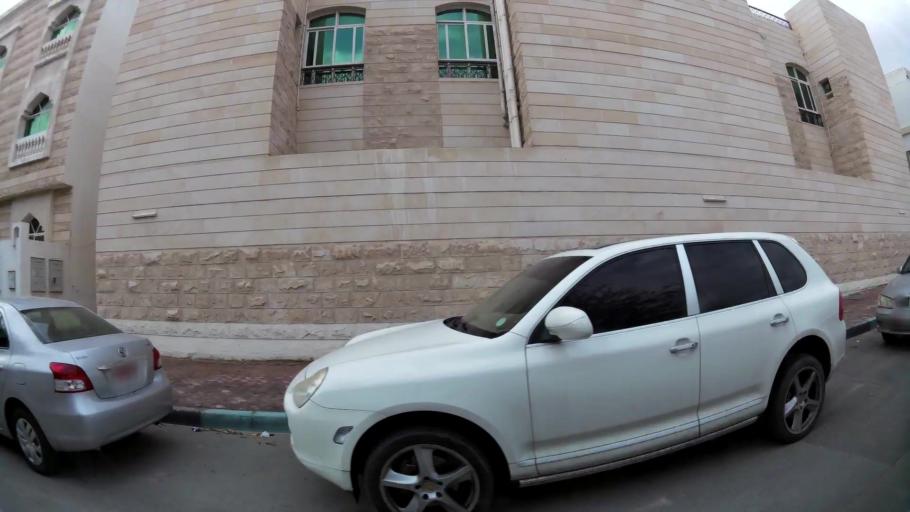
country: AE
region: Abu Dhabi
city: Abu Dhabi
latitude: 24.4445
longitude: 54.3969
